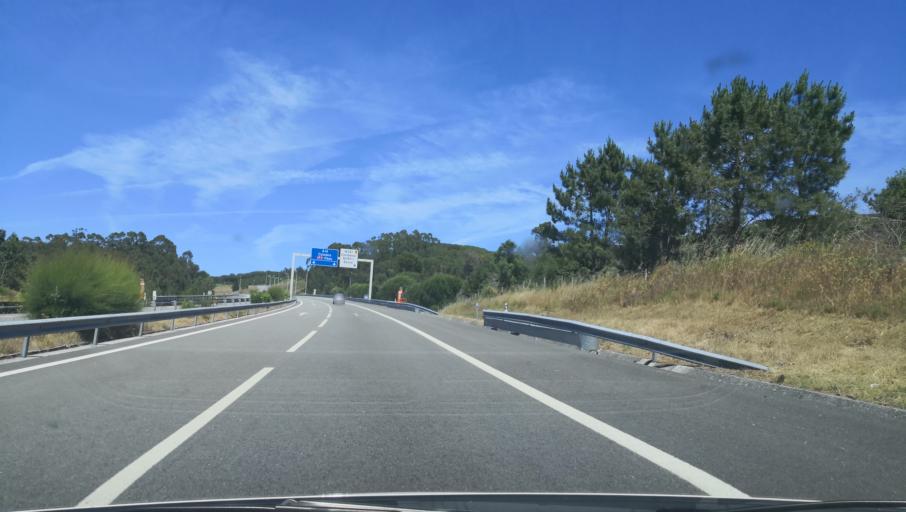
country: PT
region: Coimbra
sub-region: Montemor-O-Velho
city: Montemor-o-Velho
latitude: 40.1976
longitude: -8.6804
